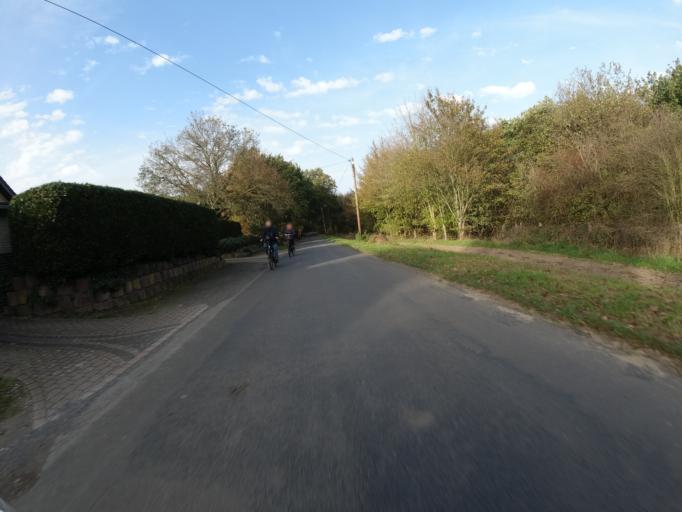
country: DE
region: North Rhine-Westphalia
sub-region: Regierungsbezirk Dusseldorf
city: Moers
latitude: 51.4088
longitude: 6.6267
